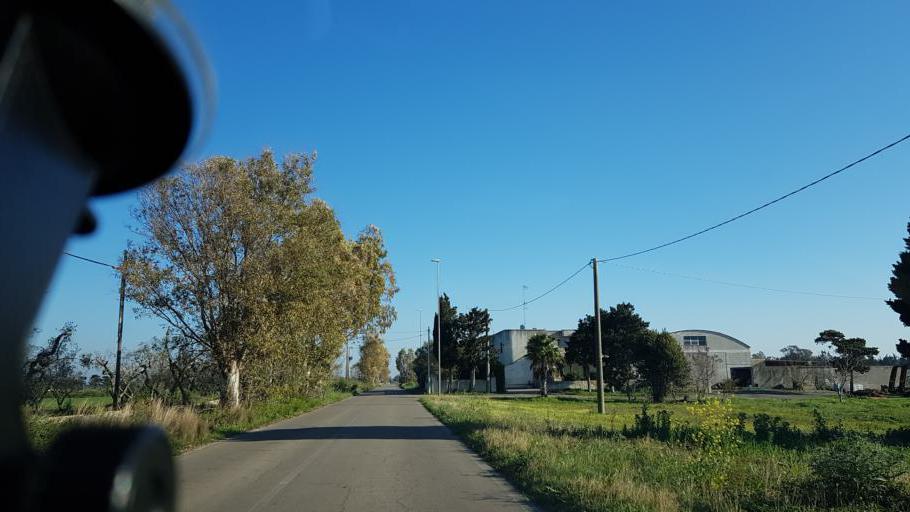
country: IT
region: Apulia
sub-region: Provincia di Lecce
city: Merine
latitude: 40.4221
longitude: 18.2474
